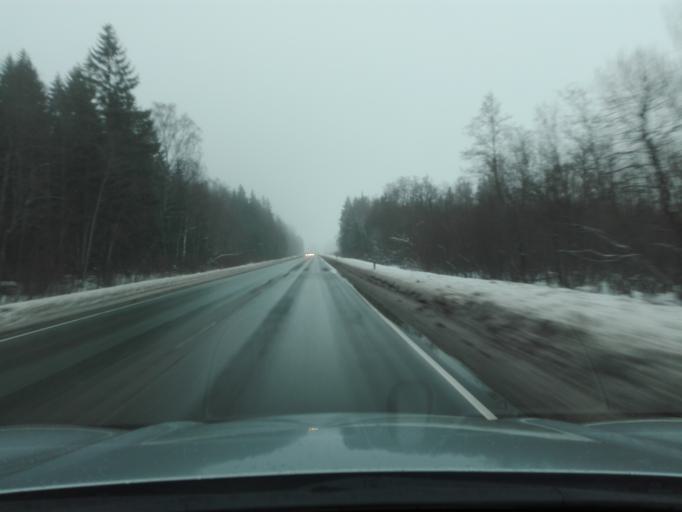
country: EE
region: Raplamaa
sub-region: Kohila vald
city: Kohila
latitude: 59.2393
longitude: 24.7595
